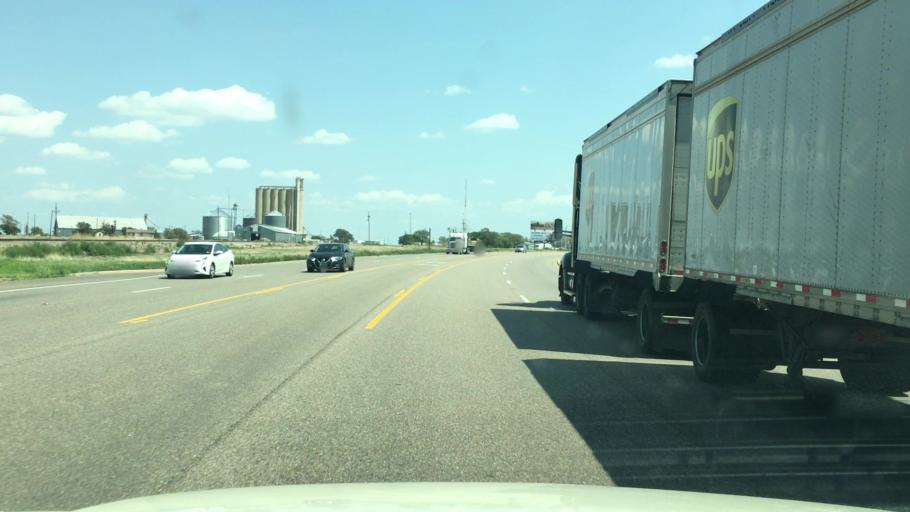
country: US
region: Texas
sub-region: Armstrong County
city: Claude
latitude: 35.1142
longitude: -101.3675
